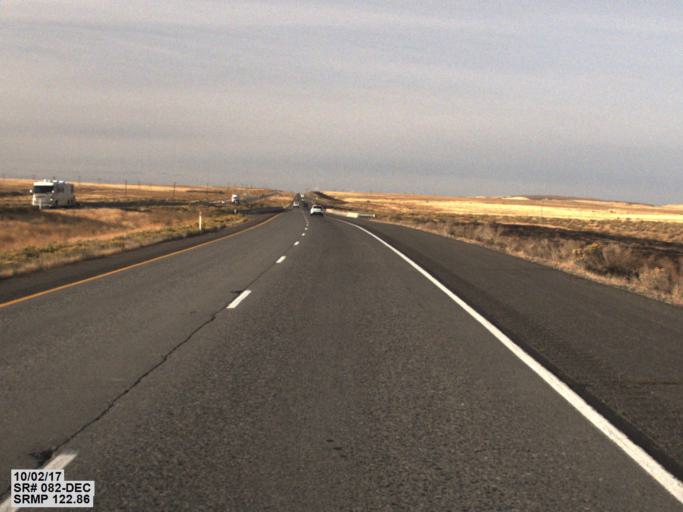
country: US
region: Washington
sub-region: Benton County
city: Highland
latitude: 46.0237
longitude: -119.2247
